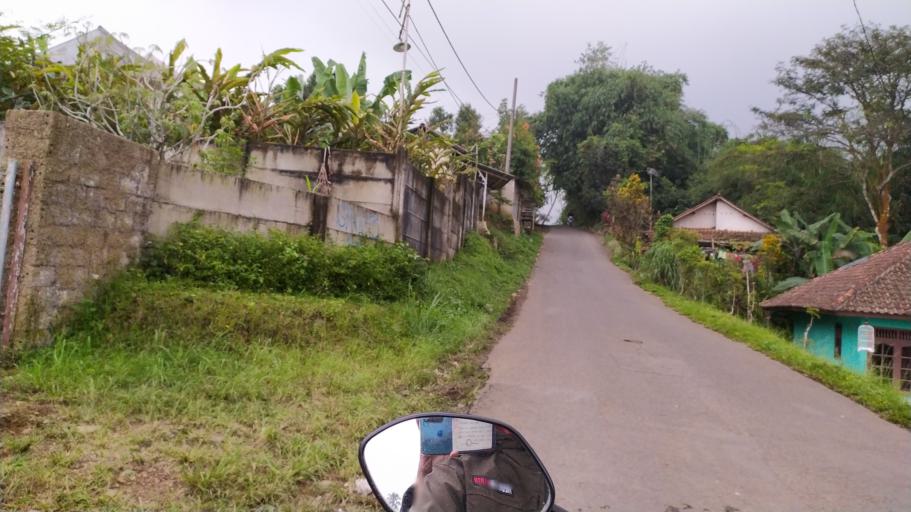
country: ID
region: West Java
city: Ciampea
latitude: -6.6530
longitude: 106.7069
